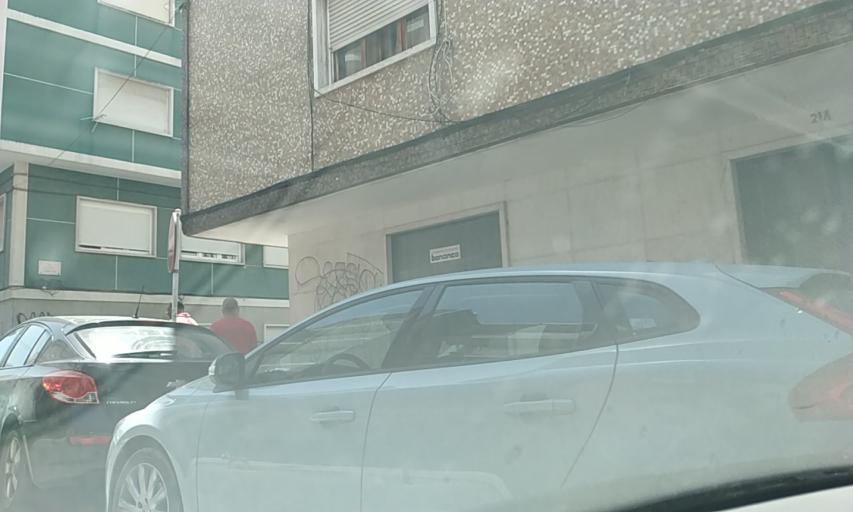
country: PT
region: Lisbon
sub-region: Loures
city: Moscavide
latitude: 38.7767
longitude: -9.1003
